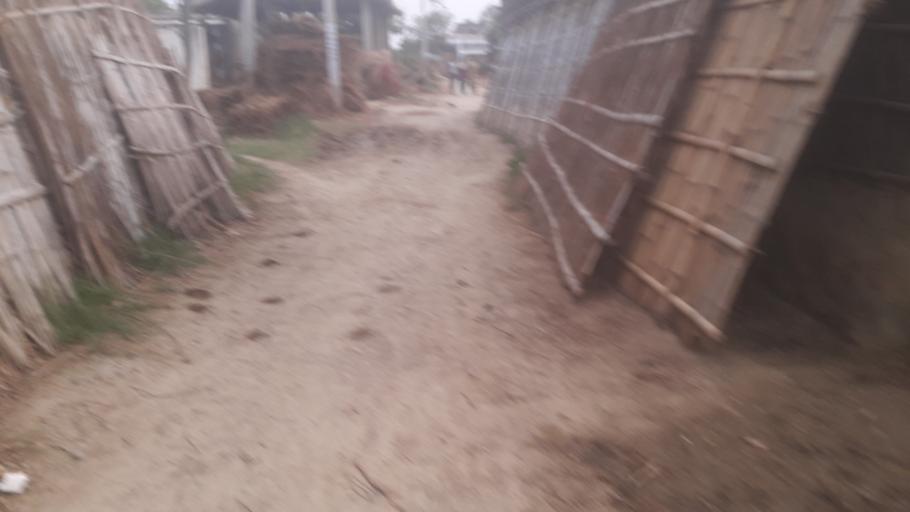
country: NP
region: Eastern Region
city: Siraha
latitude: 26.6561
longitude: 86.1963
